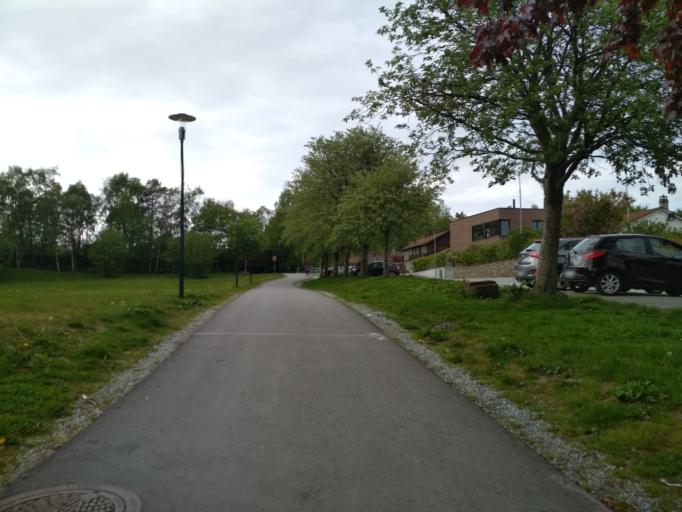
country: NO
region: Rogaland
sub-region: Stavanger
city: Stavanger
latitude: 58.9508
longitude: 5.7172
